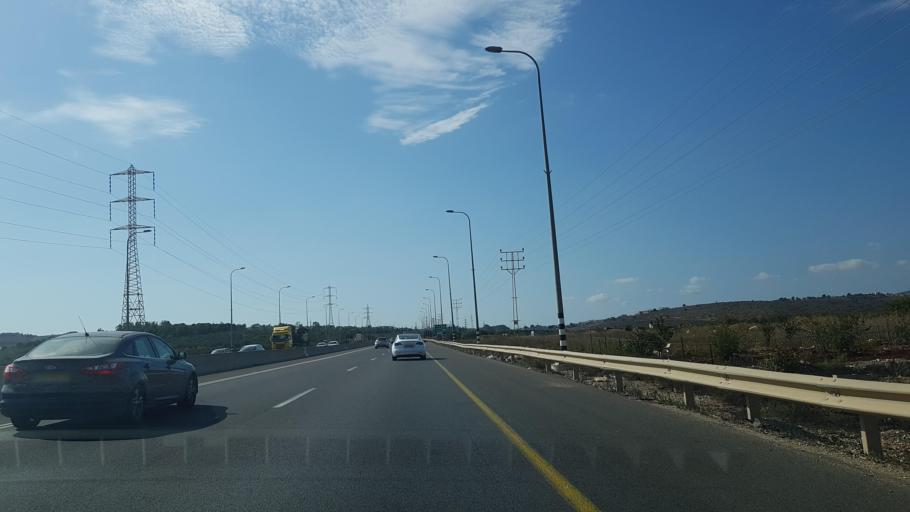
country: IL
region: Northern District
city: Kafr Kanna
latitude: 32.7633
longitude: 35.3323
